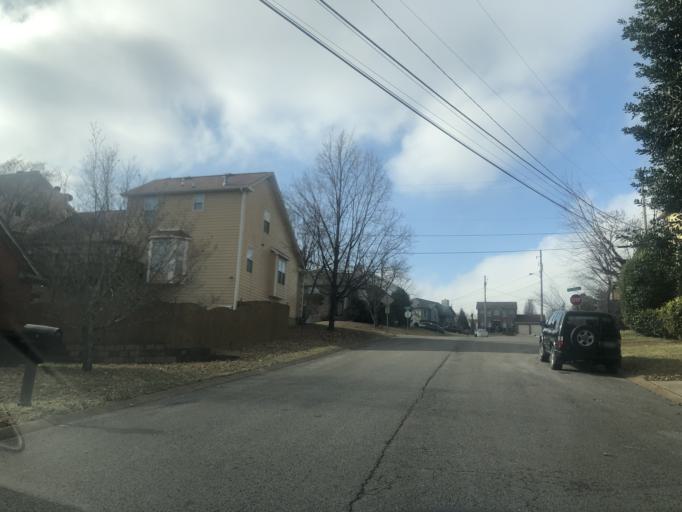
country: US
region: Tennessee
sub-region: Rutherford County
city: La Vergne
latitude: 36.0851
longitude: -86.6532
